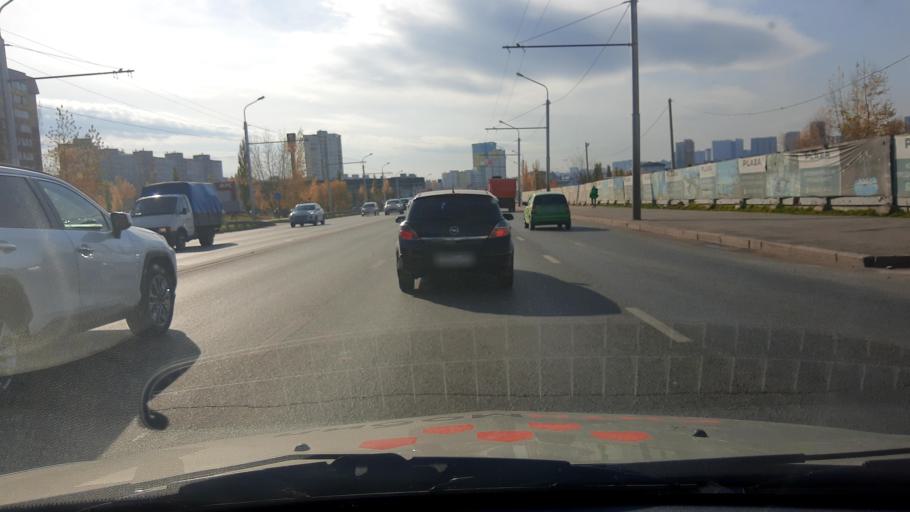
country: RU
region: Bashkortostan
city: Ufa
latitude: 54.7758
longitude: 56.0676
